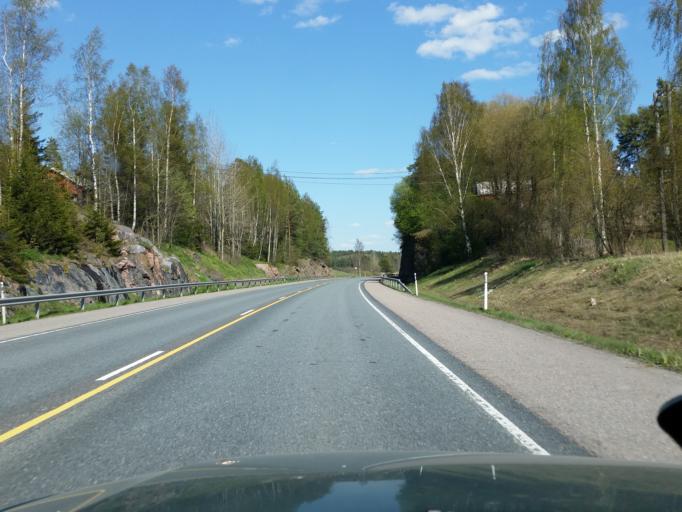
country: FI
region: Uusimaa
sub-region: Helsinki
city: Siuntio
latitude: 60.0787
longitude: 24.1471
